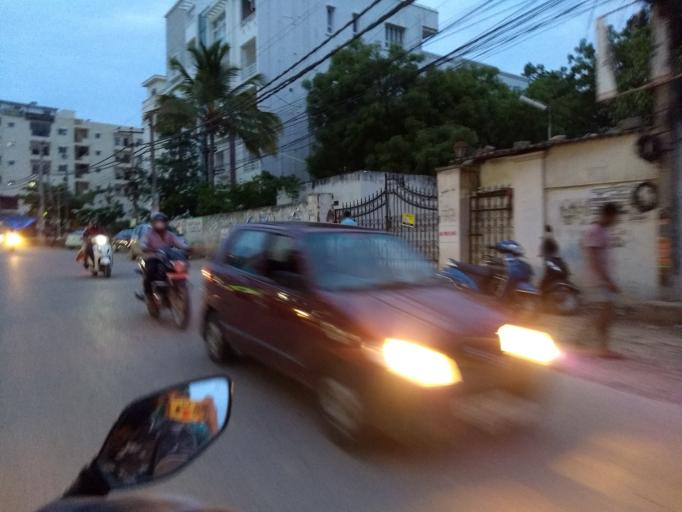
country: IN
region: Telangana
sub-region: Hyderabad
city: Hyderabad
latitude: 17.4075
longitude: 78.3828
